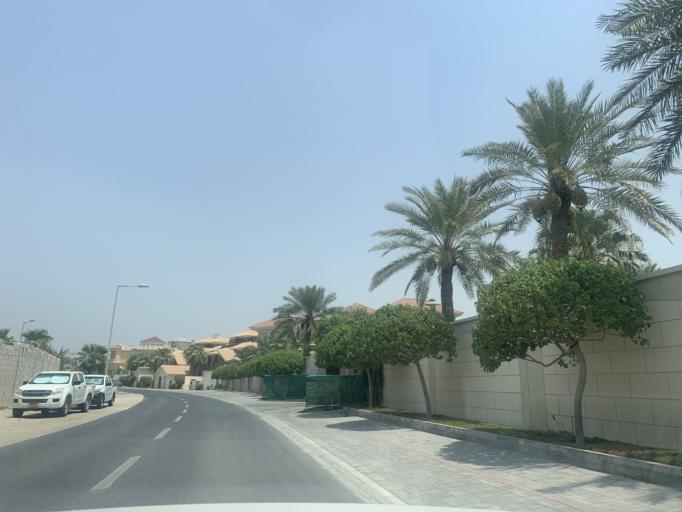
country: BH
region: Central Governorate
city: Madinat Hamad
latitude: 26.1477
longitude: 50.4727
